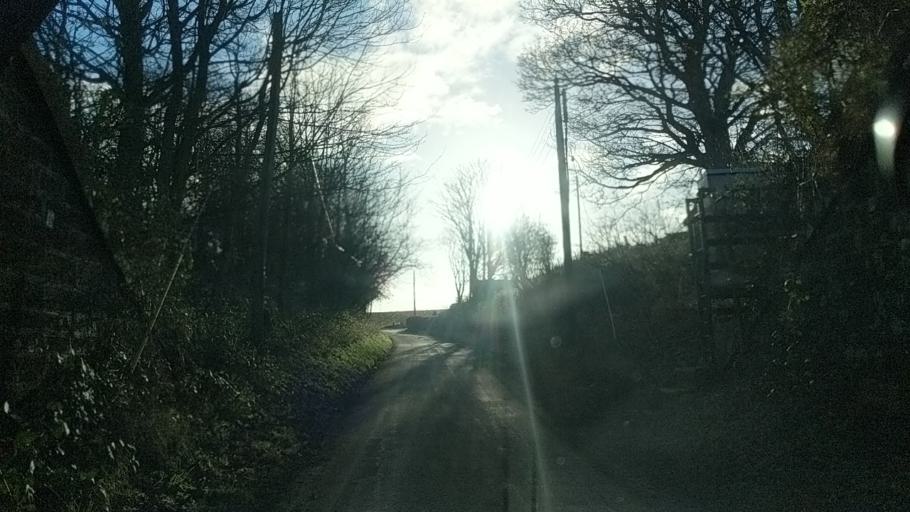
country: GB
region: Scotland
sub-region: West Lothian
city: Linlithgow
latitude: 55.9786
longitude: -3.5338
